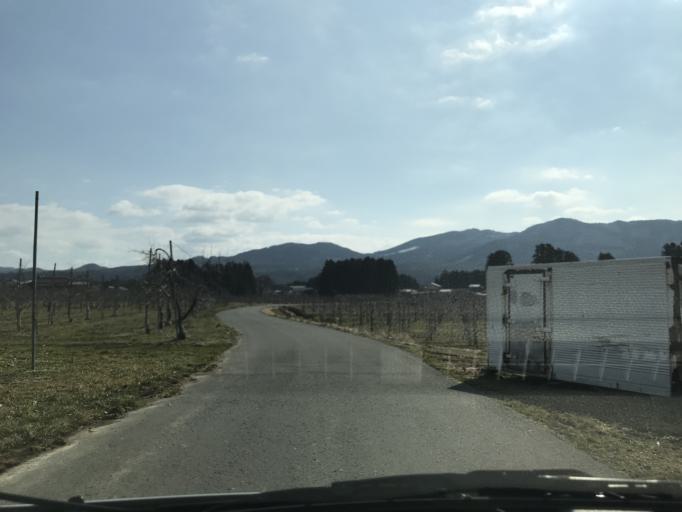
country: JP
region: Iwate
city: Mizusawa
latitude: 39.0425
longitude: 141.1365
